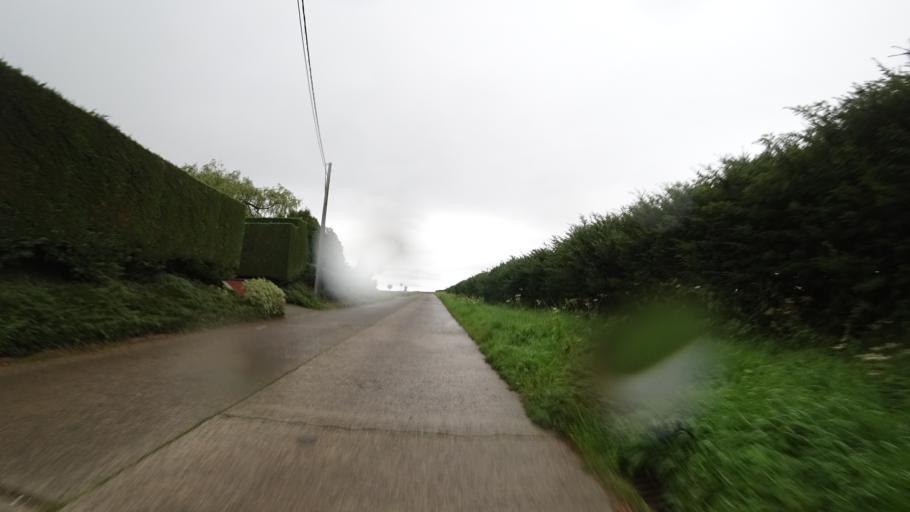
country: BE
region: Wallonia
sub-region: Province de Namur
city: Gembloux
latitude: 50.5681
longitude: 4.7356
